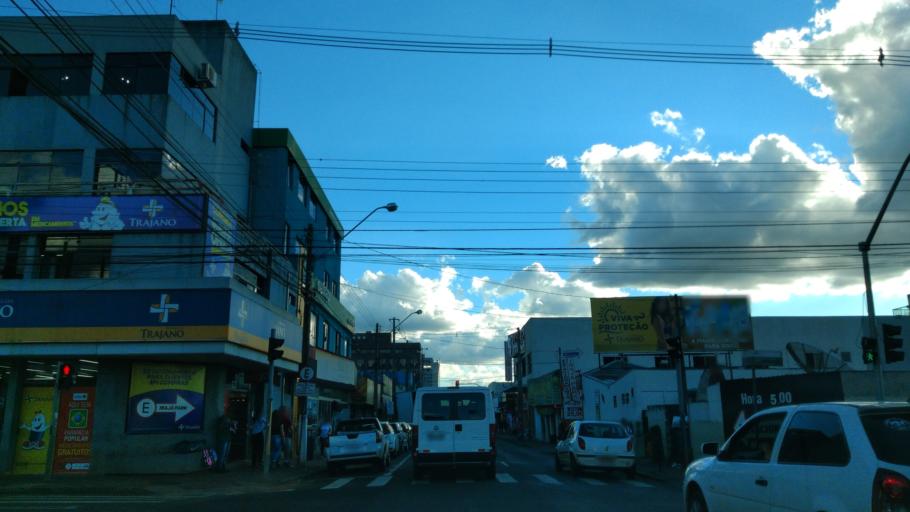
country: BR
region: Parana
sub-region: Guarapuava
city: Guarapuava
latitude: -25.3925
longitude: -51.4683
